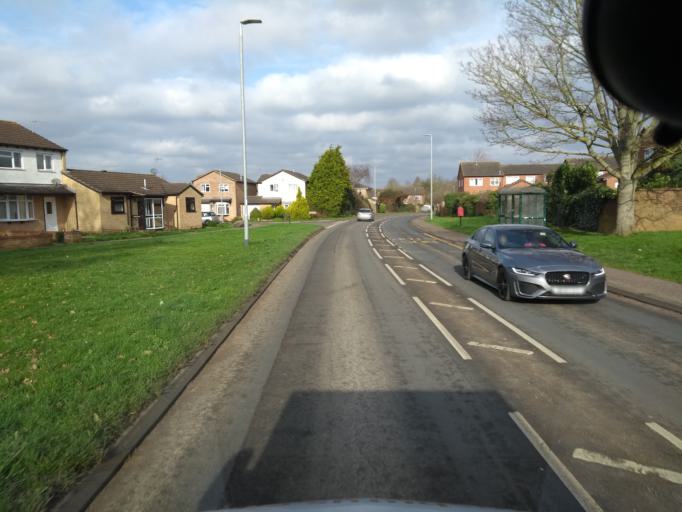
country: GB
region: England
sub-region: Somerset
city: Taunton
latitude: 51.0023
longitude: -3.0823
